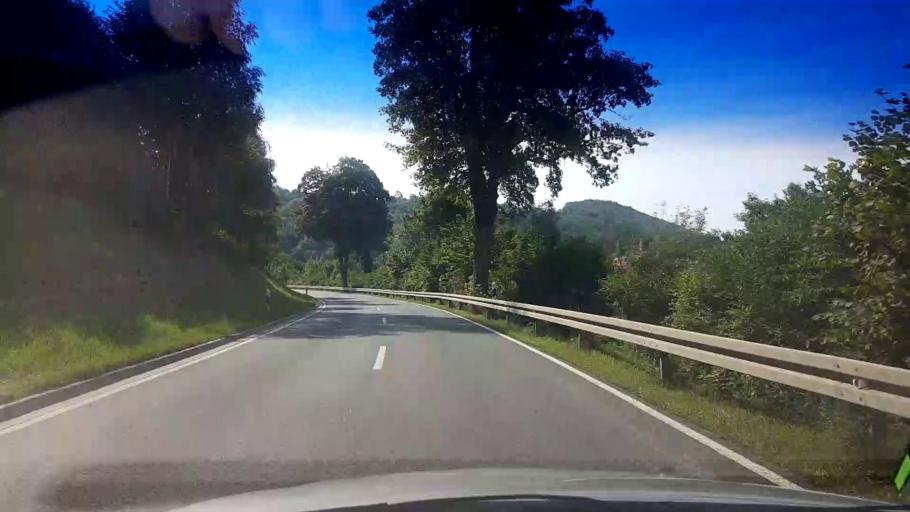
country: DE
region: Bavaria
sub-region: Upper Franconia
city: Hollfeld
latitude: 49.9364
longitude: 11.3450
